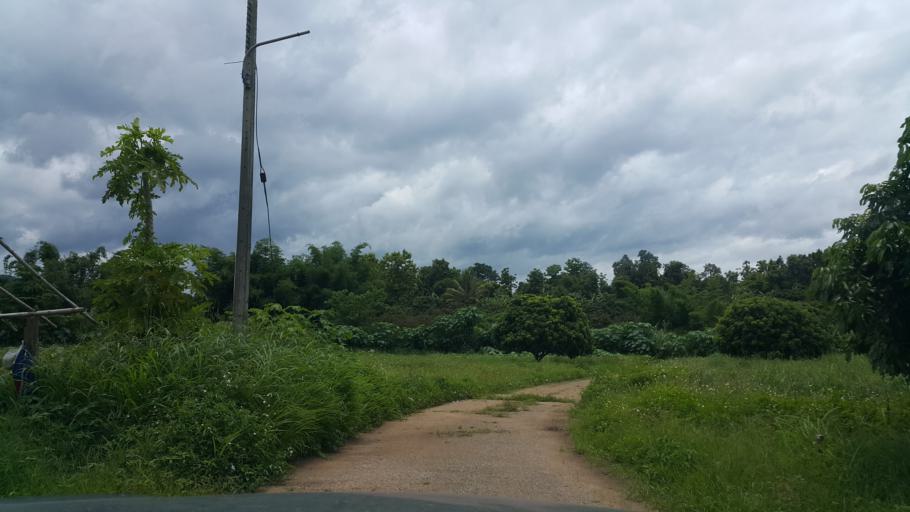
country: TH
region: Chiang Mai
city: Mae Taeng
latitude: 19.1986
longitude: 98.9859
